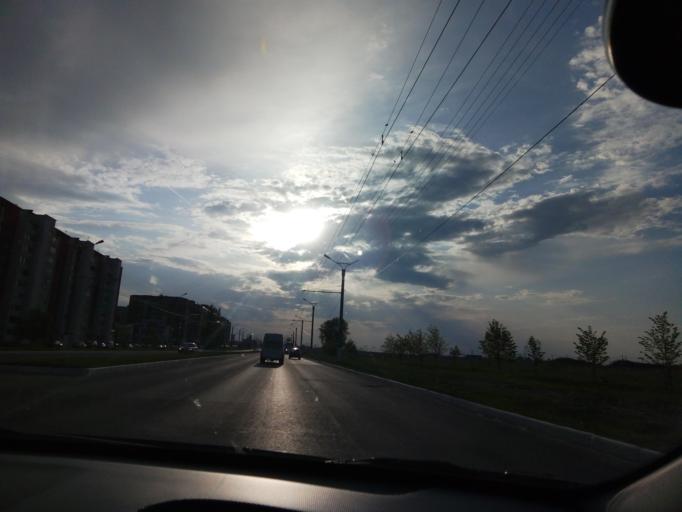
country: RU
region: Chuvashia
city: Novocheboksarsk
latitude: 56.1197
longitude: 47.4565
